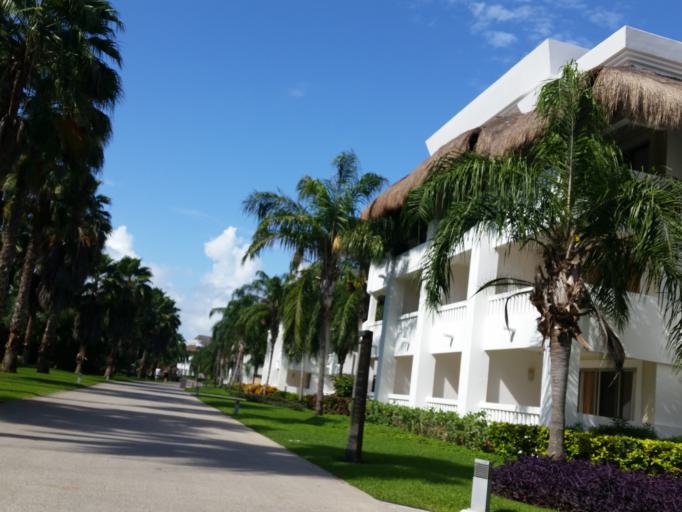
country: MX
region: Quintana Roo
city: Playa del Carmen
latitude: 20.6688
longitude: -87.0309
